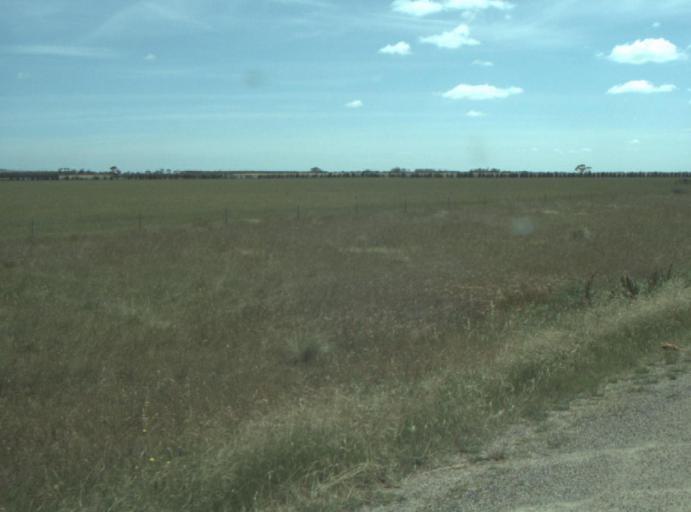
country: AU
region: Victoria
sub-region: Wyndham
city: Little River
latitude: -38.0078
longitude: 144.4622
